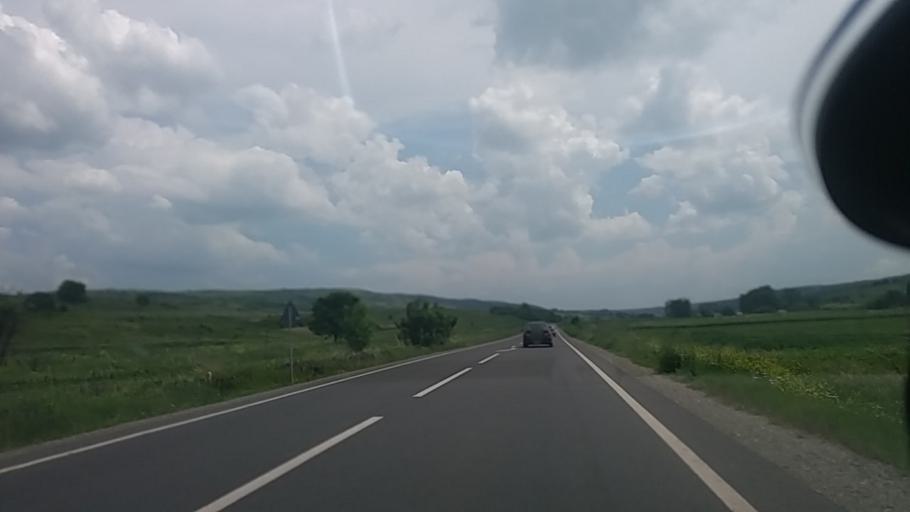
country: RO
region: Sibiu
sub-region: Comuna Seica Mare
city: Seica Mare
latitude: 45.9731
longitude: 24.1481
